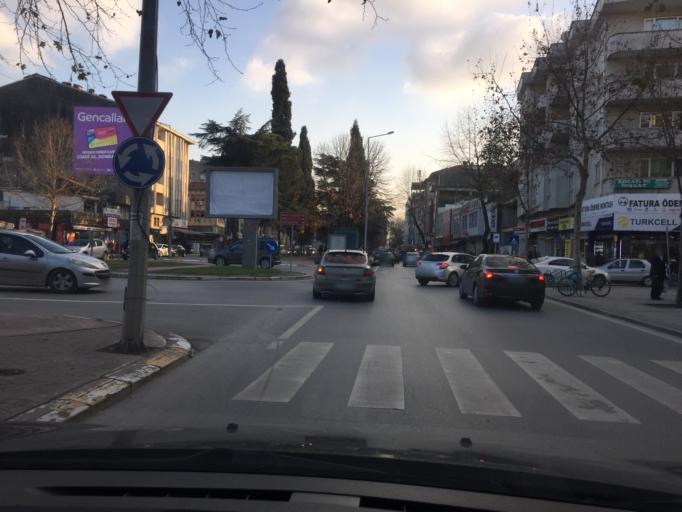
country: TR
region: Sakarya
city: Adapazari
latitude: 40.7833
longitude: 30.3997
